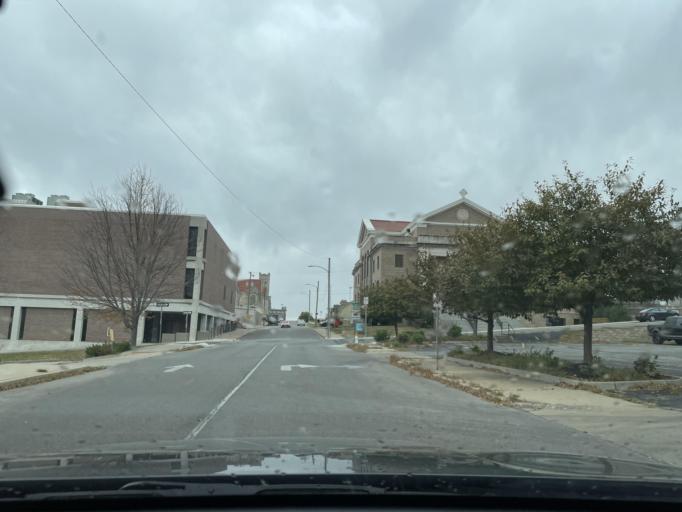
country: US
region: Missouri
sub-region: Buchanan County
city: Saint Joseph
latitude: 39.7692
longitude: -94.8476
